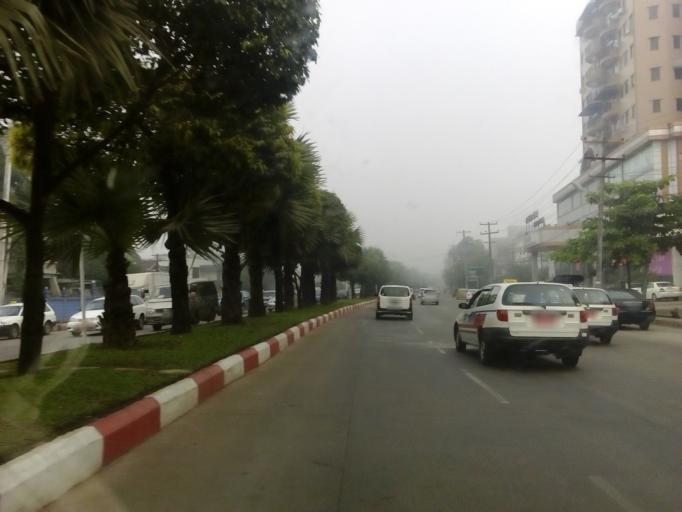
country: MM
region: Yangon
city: Yangon
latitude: 16.8236
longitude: 96.1813
